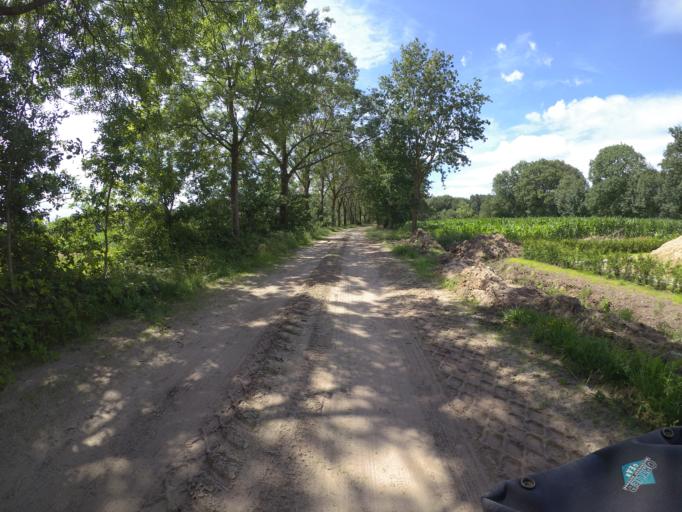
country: NL
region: North Brabant
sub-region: Gemeente Haaren
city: Haaren
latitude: 51.6033
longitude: 5.2712
